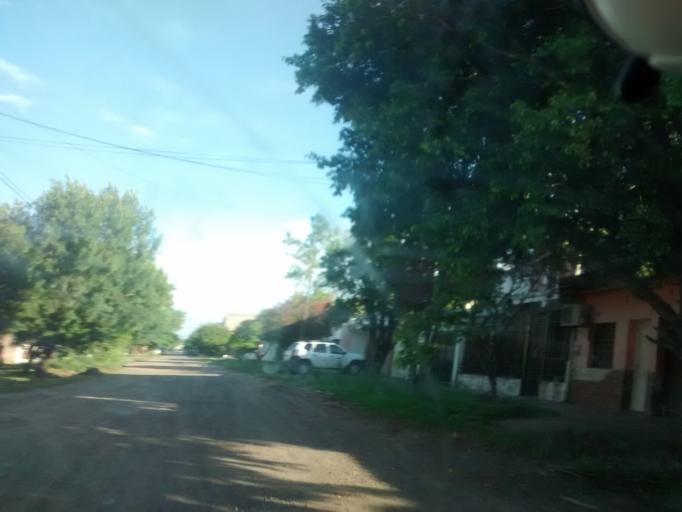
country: AR
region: Chaco
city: Resistencia
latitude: -27.4669
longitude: -58.9958
